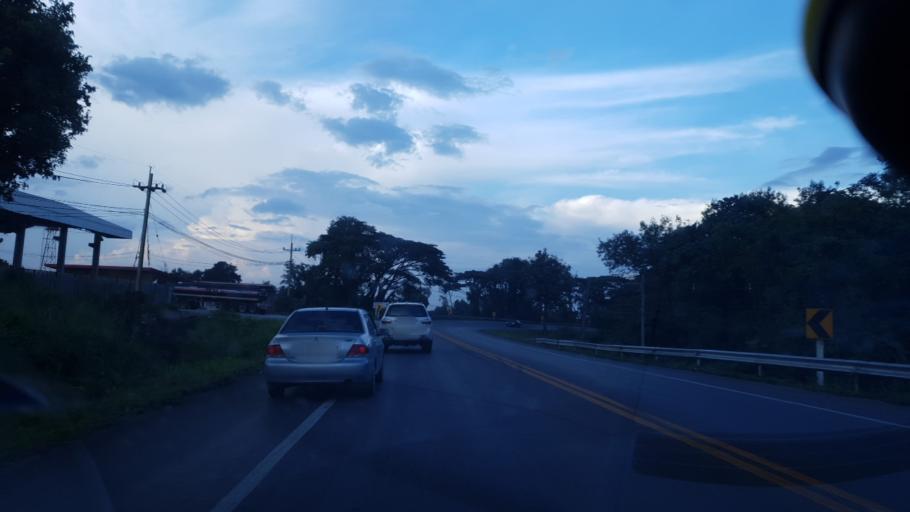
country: TH
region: Chiang Rai
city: Mae Lao
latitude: 19.7462
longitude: 99.6775
